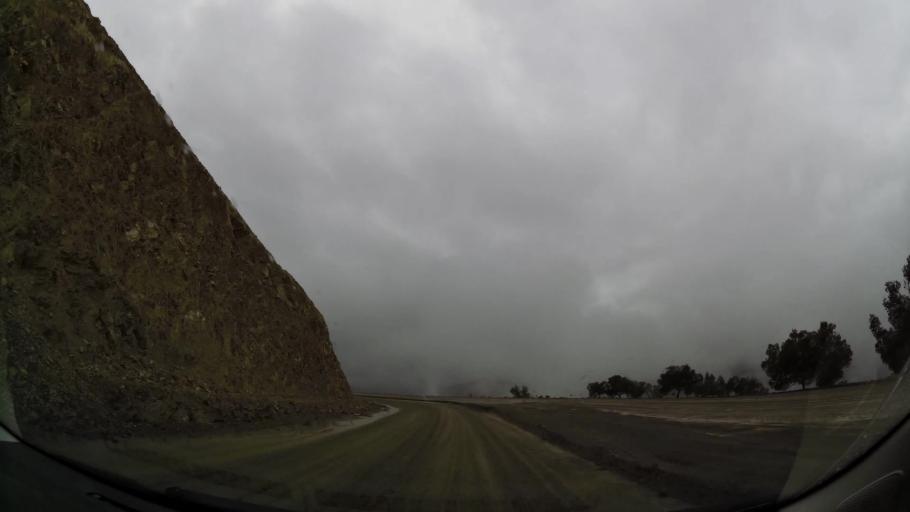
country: MA
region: Taza-Al Hoceima-Taounate
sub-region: Taza
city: Ajdir
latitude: 34.8987
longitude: -3.7837
